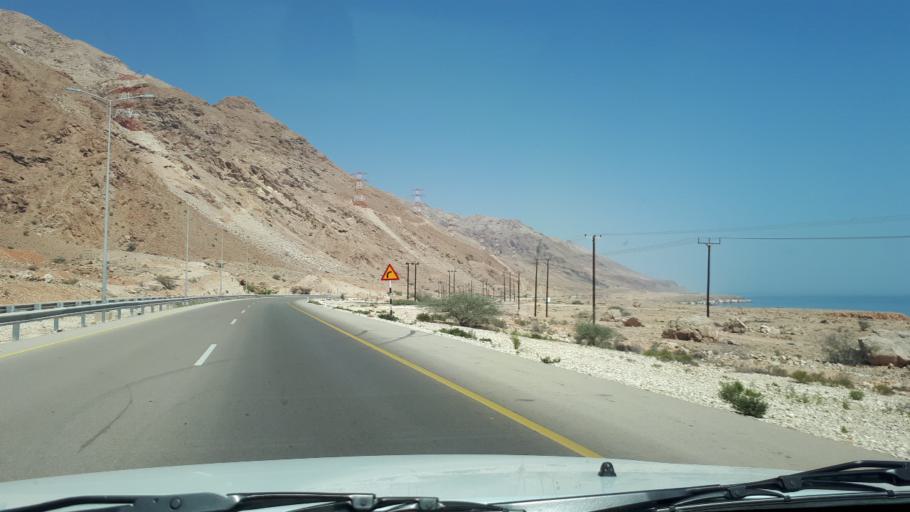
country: OM
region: Ash Sharqiyah
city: Sur
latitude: 22.7602
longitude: 59.2930
